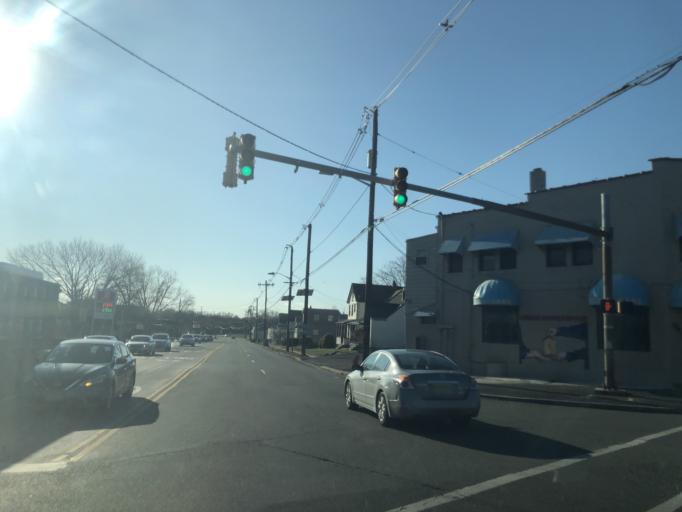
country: US
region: New Jersey
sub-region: Middlesex County
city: Fords
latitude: 40.5312
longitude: -74.3256
